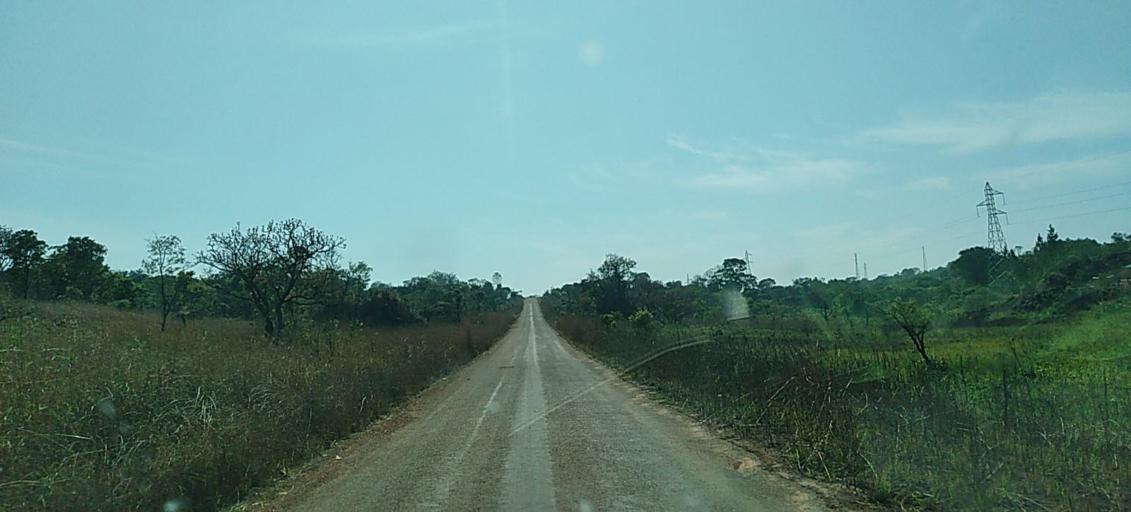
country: ZM
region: North-Western
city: Mwinilunga
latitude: -11.8257
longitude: 25.1303
